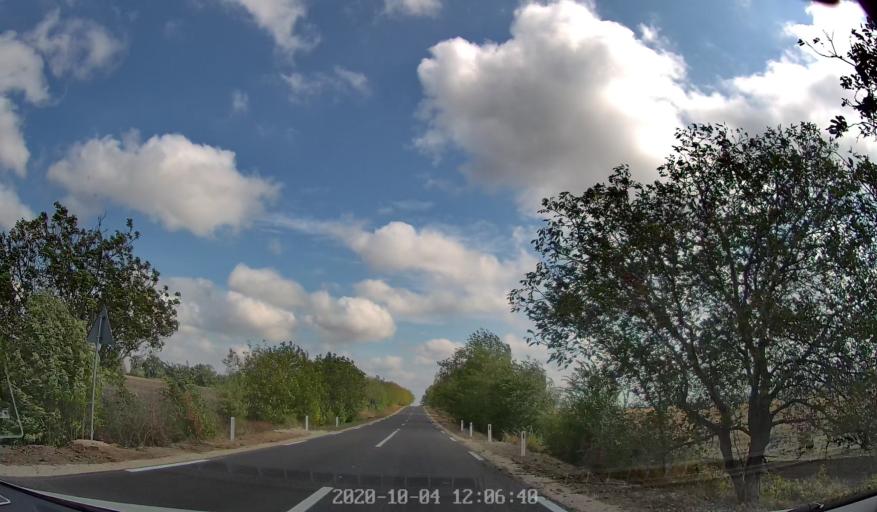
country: MD
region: Rezina
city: Saharna
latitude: 47.5834
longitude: 28.9602
